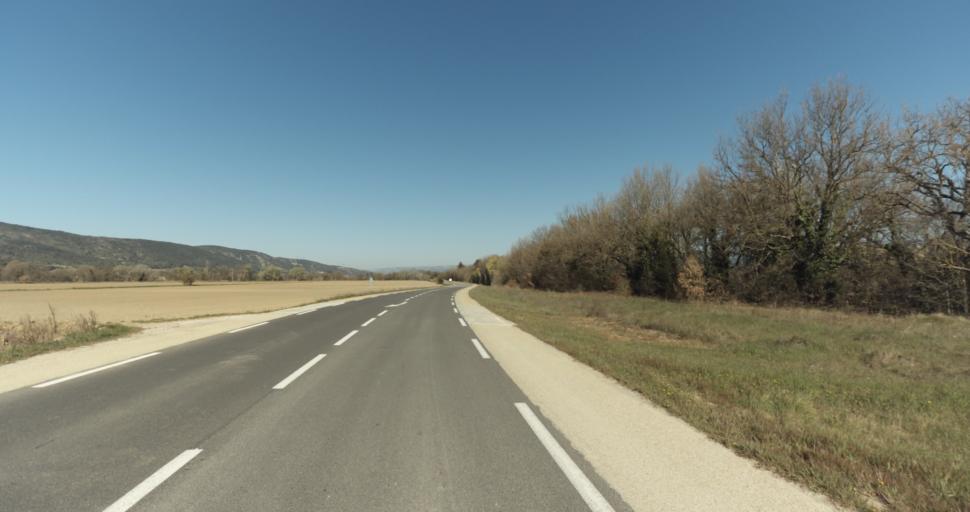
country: FR
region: Provence-Alpes-Cote d'Azur
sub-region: Departement des Bouches-du-Rhone
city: Le Puy-Sainte-Reparade
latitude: 43.6725
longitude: 5.4290
